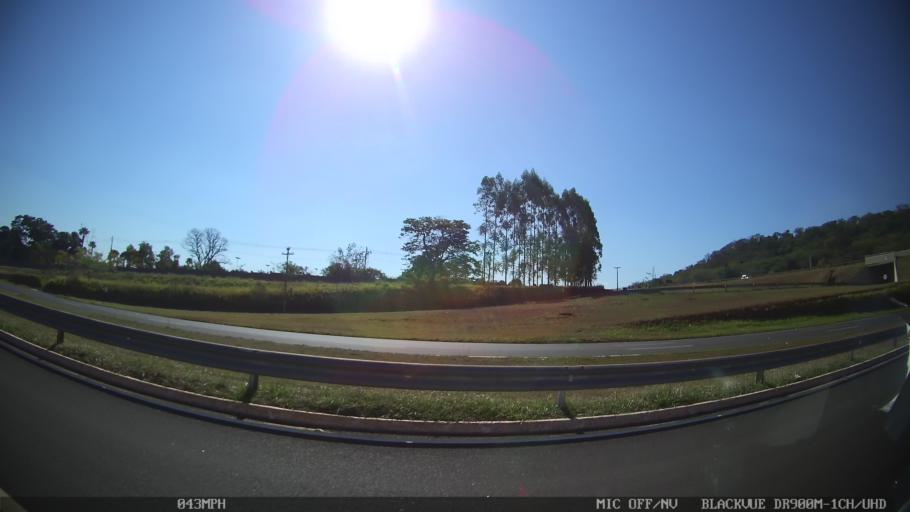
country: BR
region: Sao Paulo
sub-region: Ribeirao Preto
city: Ribeirao Preto
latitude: -21.2377
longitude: -47.7597
